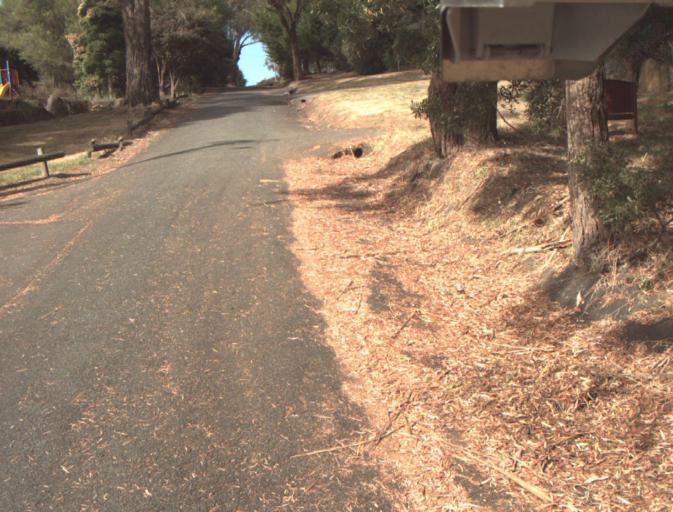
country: AU
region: Tasmania
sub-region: Launceston
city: West Launceston
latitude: -41.4575
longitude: 147.1310
